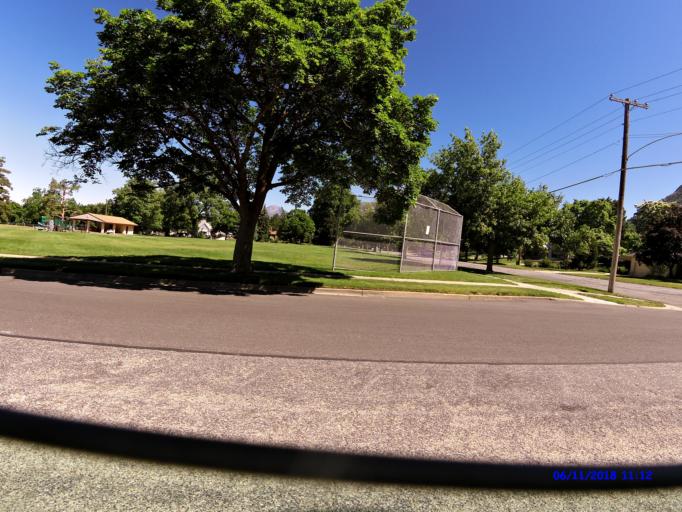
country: US
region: Utah
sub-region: Weber County
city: Ogden
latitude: 41.2202
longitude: -111.9375
